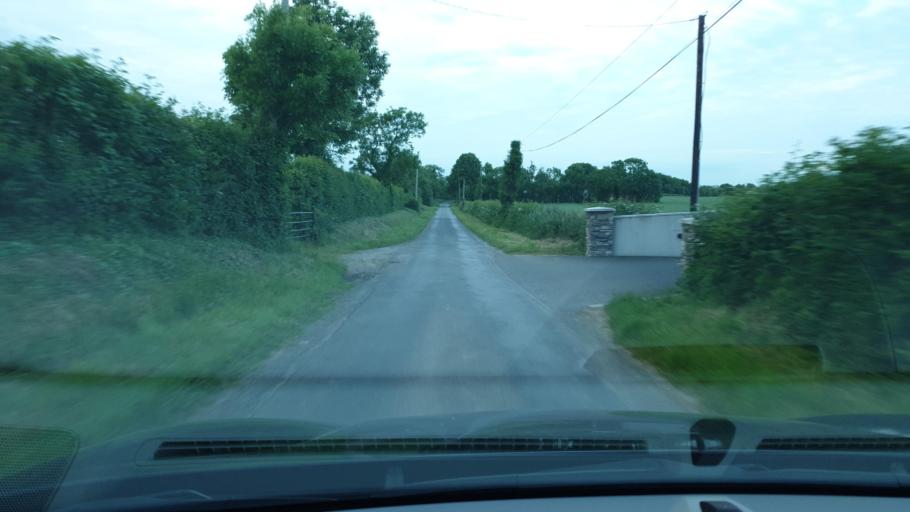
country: IE
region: Leinster
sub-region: An Mhi
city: Ashbourne
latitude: 53.4778
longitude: -6.3539
